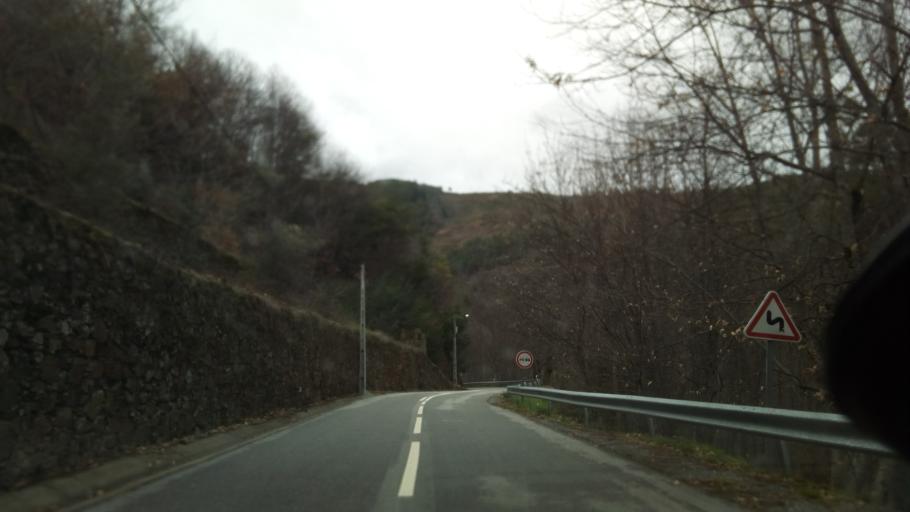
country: PT
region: Guarda
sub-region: Manteigas
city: Manteigas
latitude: 40.4089
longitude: -7.5272
